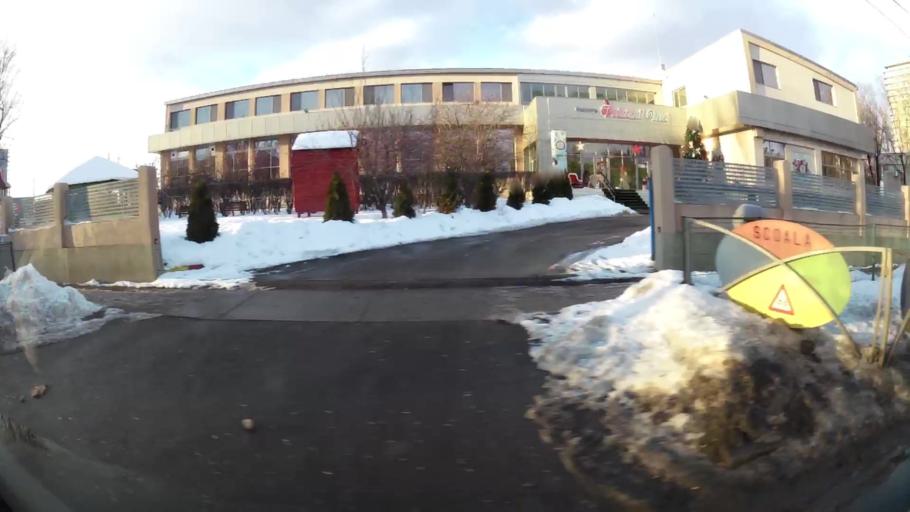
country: RO
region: Ilfov
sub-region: Comuna Popesti-Leordeni
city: Popesti-Leordeni
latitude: 44.3694
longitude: 26.1382
